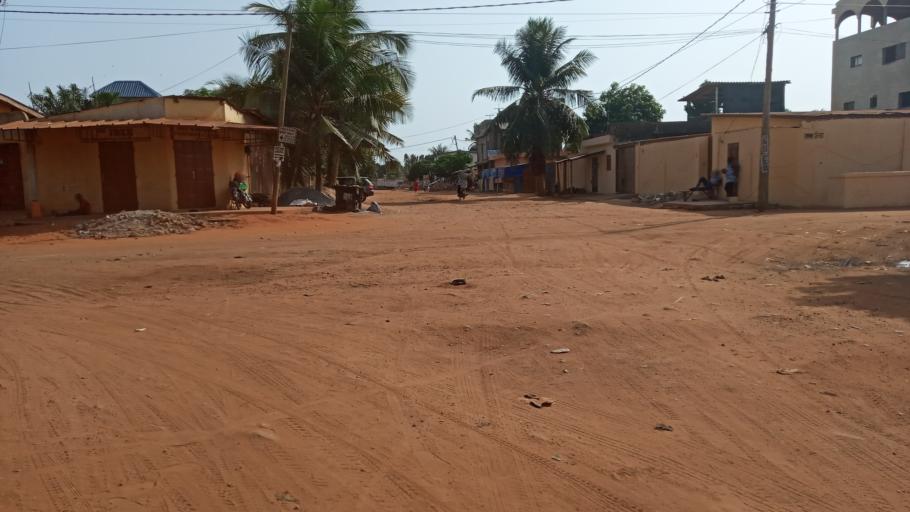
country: TG
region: Maritime
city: Lome
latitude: 6.2343
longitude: 1.1949
